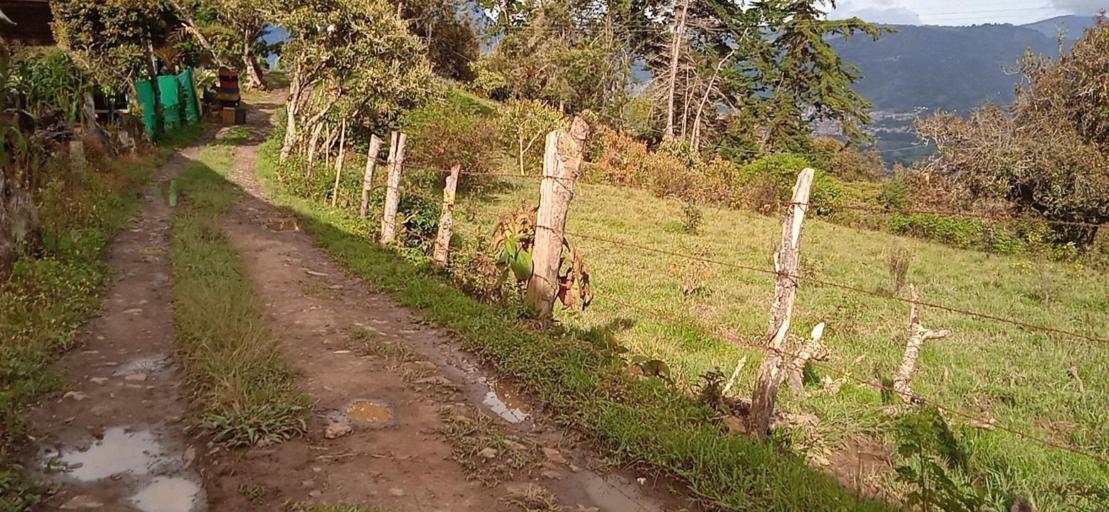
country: CO
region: Cundinamarca
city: Tenza
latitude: 5.0960
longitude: -73.4097
